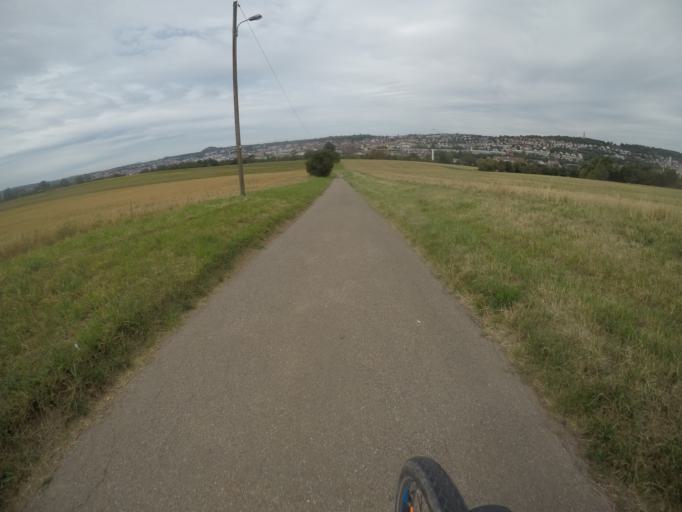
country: DE
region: Baden-Wuerttemberg
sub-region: Karlsruhe Region
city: Pforzheim
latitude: 48.8880
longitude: 8.7240
